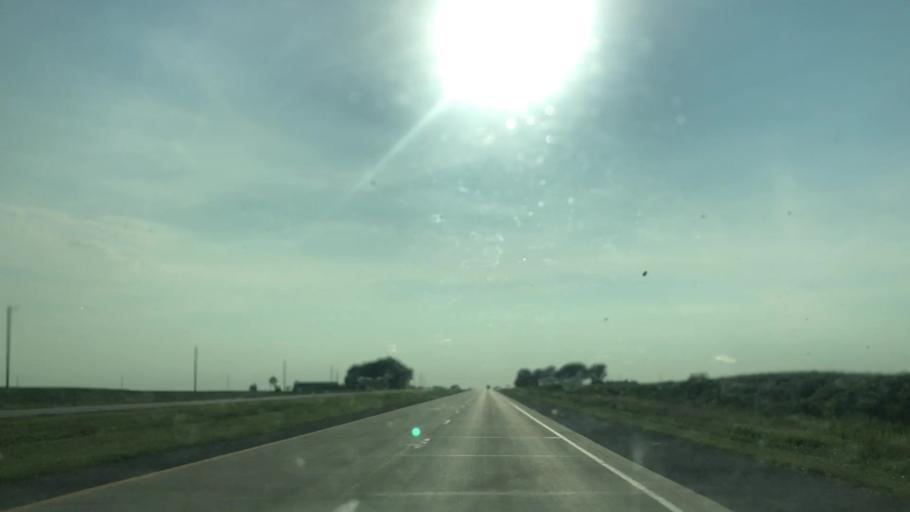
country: US
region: Iowa
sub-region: Story County
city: Nevada
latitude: 42.0079
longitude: -93.3975
